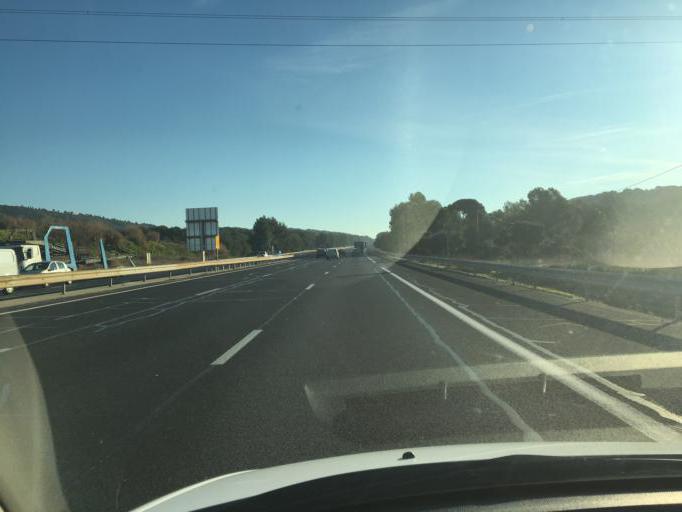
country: FR
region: Provence-Alpes-Cote d'Azur
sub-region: Departement des Bouches-du-Rhone
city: Coudoux
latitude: 43.5546
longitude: 5.2685
